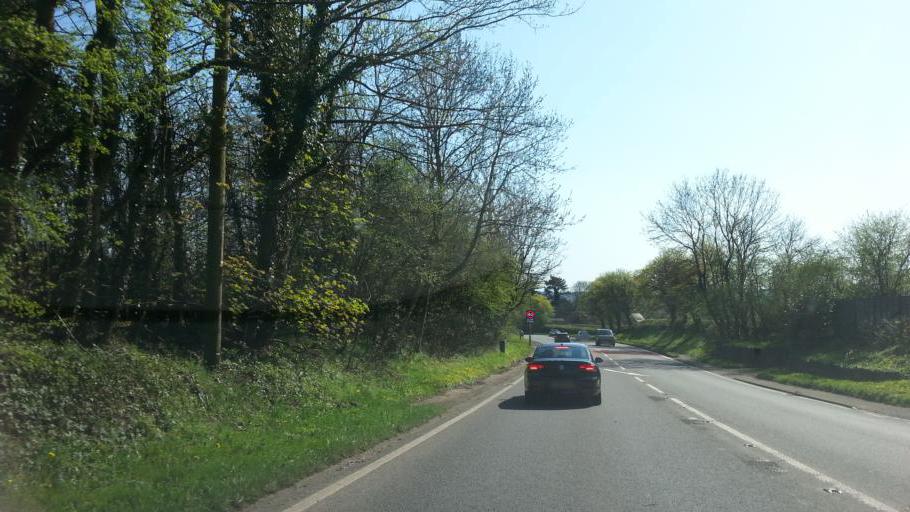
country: GB
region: England
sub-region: Worcestershire
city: Alvechurch
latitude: 52.3800
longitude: -1.9583
